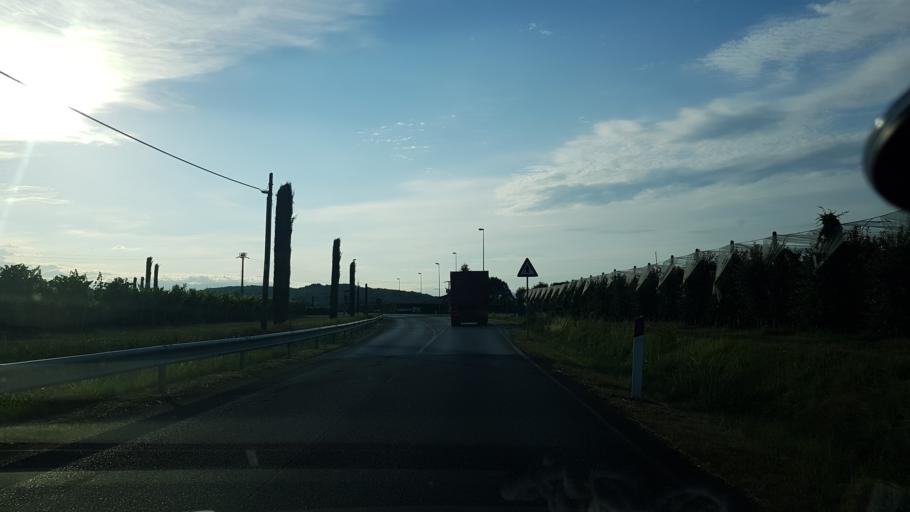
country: IT
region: Friuli Venezia Giulia
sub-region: Provincia di Udine
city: Chiopris
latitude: 45.9227
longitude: 13.3897
